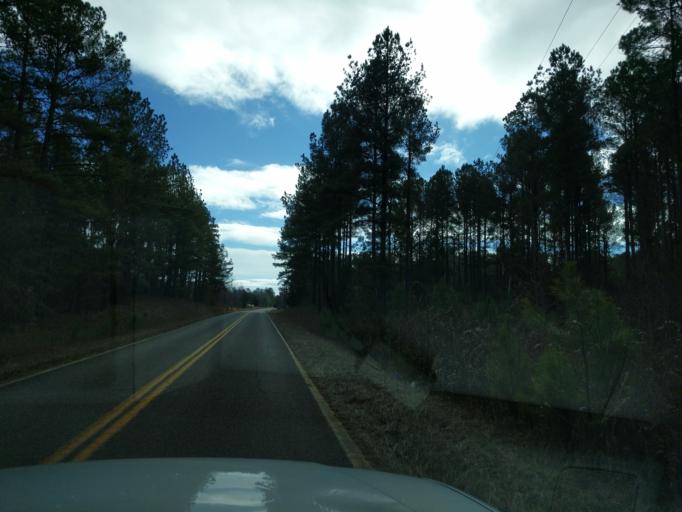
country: US
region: South Carolina
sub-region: Edgefield County
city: Edgefield
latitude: 33.8771
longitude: -81.9981
